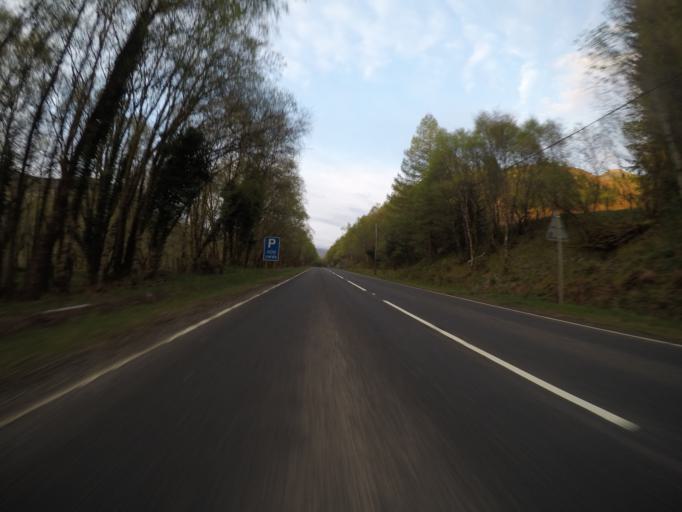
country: GB
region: Scotland
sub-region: Argyll and Bute
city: Garelochhead
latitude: 56.3931
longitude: -4.5897
